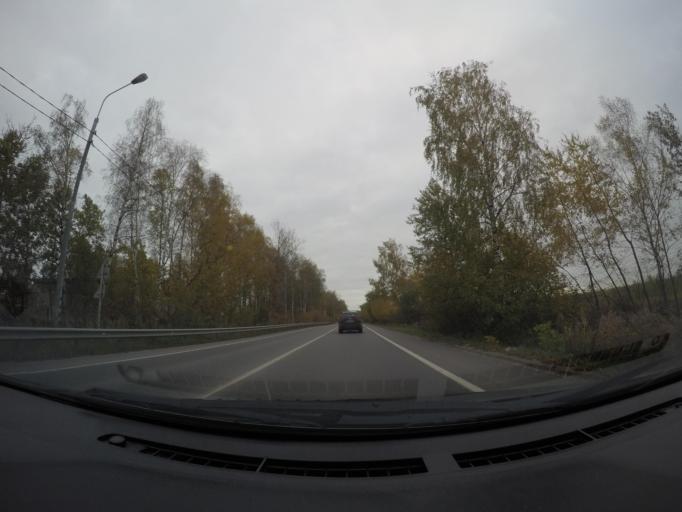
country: RU
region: Moskovskaya
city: Imeni Vorovskogo
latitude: 55.7281
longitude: 38.2735
